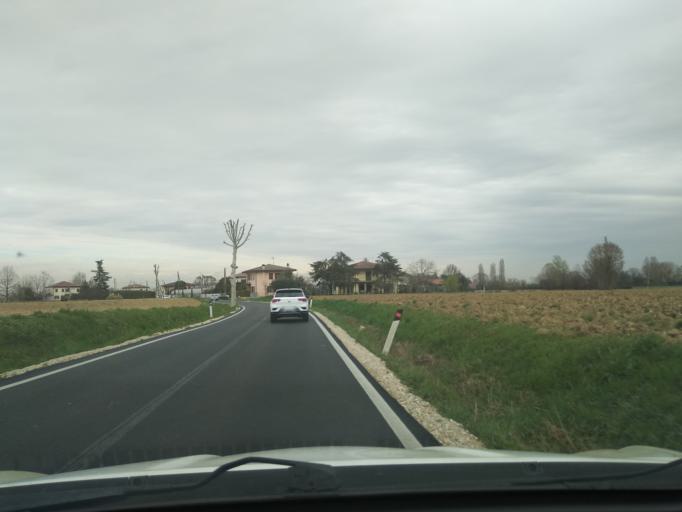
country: IT
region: Veneto
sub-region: Provincia di Padova
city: Rubano
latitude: 45.4082
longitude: 11.7853
